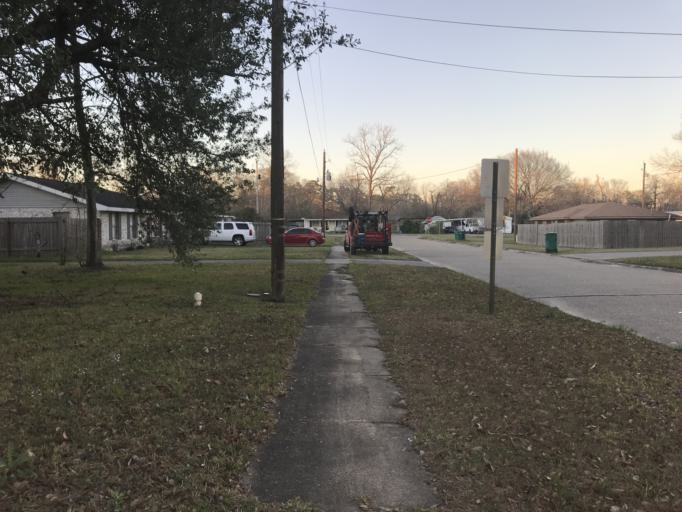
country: US
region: Louisiana
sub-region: Calcasieu Parish
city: Westlake
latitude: 30.2561
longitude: -93.2556
